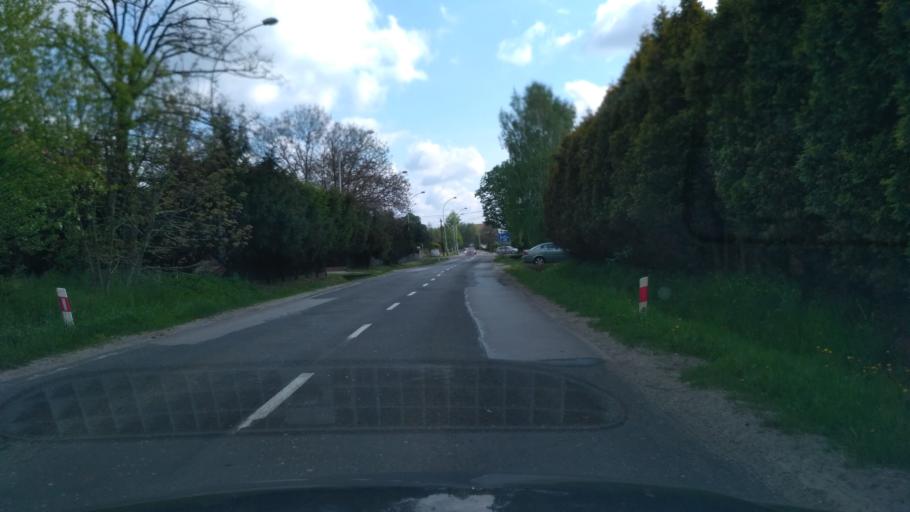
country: PL
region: Subcarpathian Voivodeship
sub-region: Powiat przeworski
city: Przeworsk
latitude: 50.0489
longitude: 22.4874
